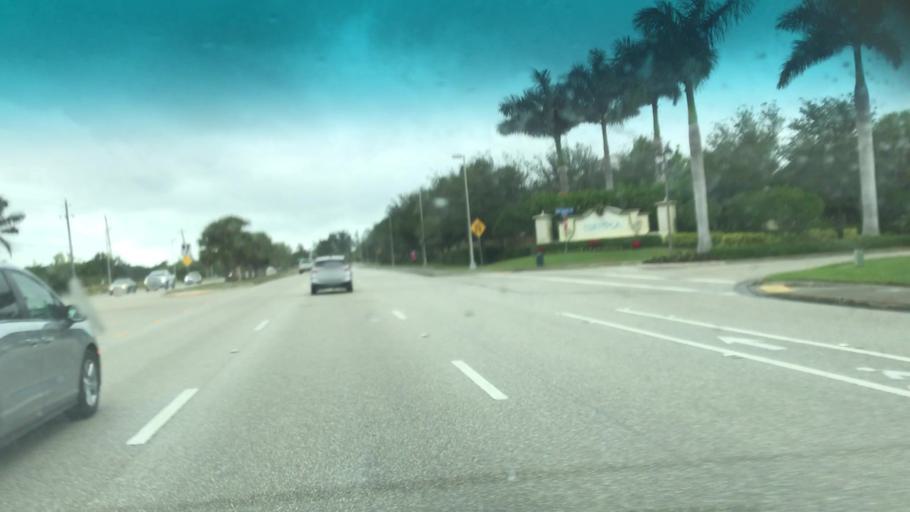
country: US
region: Florida
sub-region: Lee County
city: Harlem Heights
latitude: 26.5204
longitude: -81.9153
